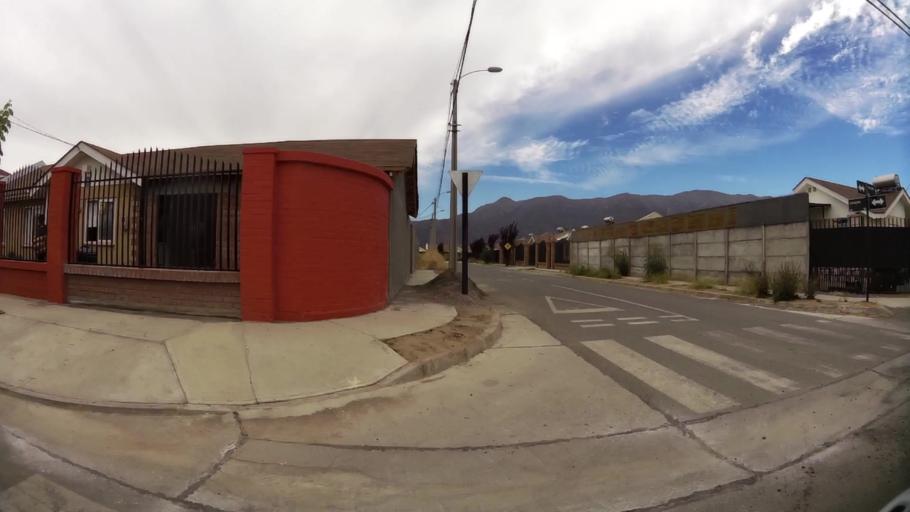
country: CL
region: O'Higgins
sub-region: Provincia de Cachapoal
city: Graneros
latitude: -34.0806
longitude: -70.7375
